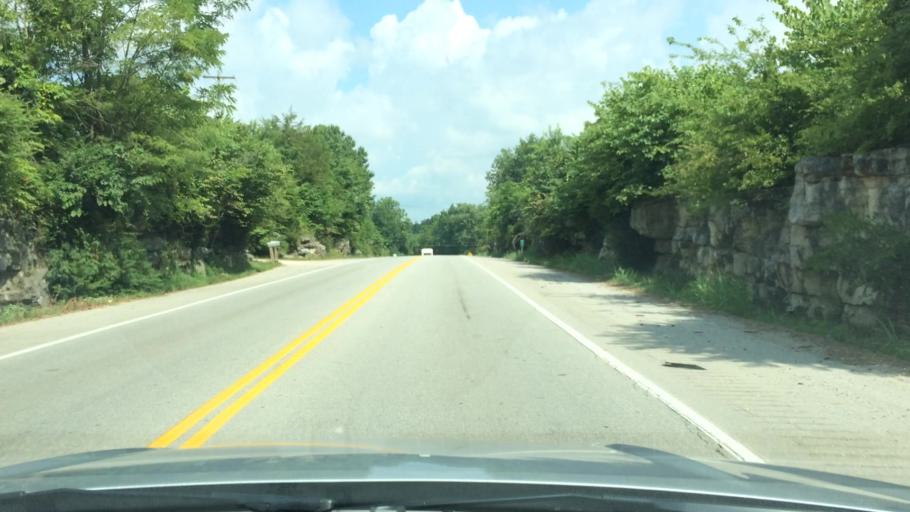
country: US
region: Kentucky
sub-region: Pulaski County
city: Somerset
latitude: 36.9674
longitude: -84.5872
